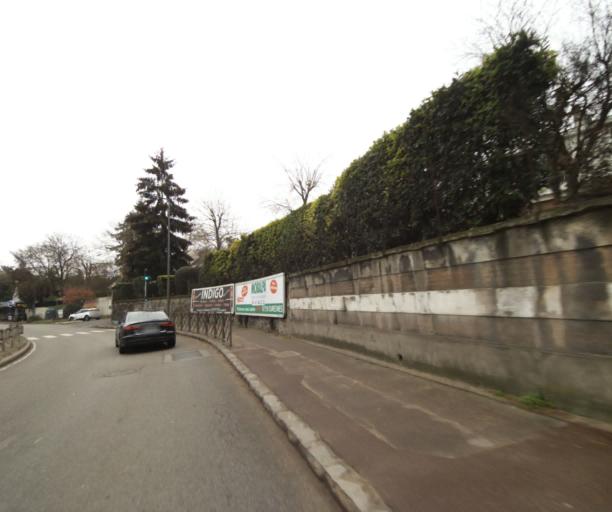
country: FR
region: Ile-de-France
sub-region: Departement des Yvelines
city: Bougival
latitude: 48.8682
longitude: 2.1519
